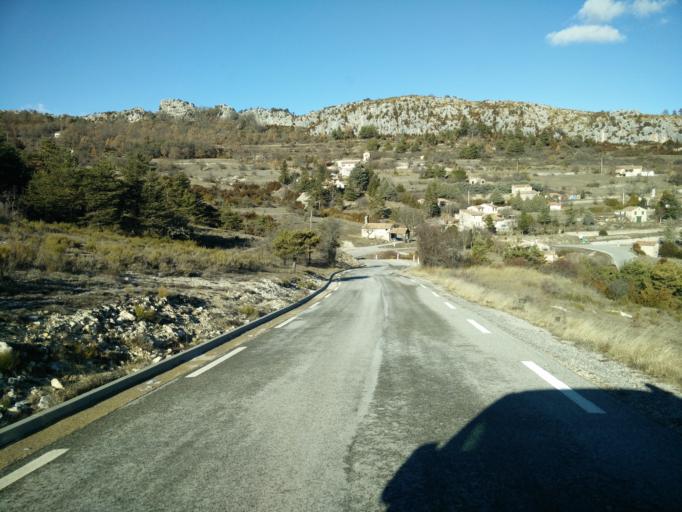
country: FR
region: Provence-Alpes-Cote d'Azur
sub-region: Departement des Alpes-de-Haute-Provence
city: Castellane
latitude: 43.7582
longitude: 6.4411
